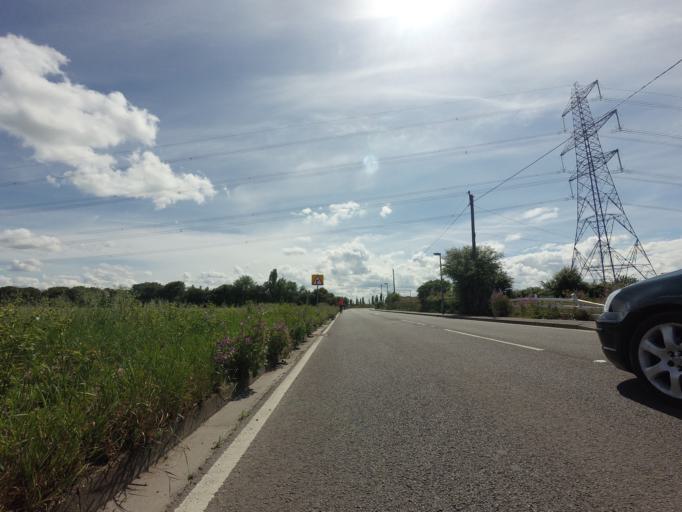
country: GB
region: England
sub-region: Kent
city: Sheerness
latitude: 51.4549
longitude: 0.7089
